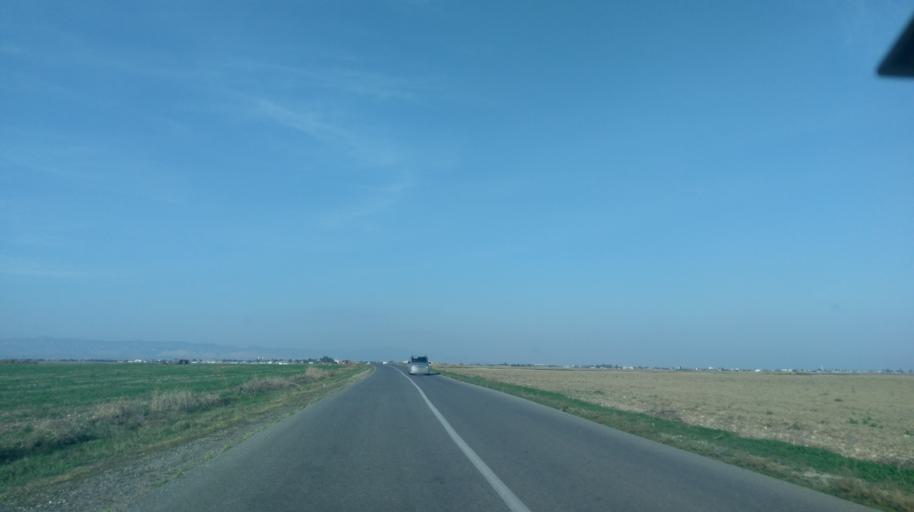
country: CY
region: Ammochostos
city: Achna
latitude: 35.1480
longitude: 33.7483
